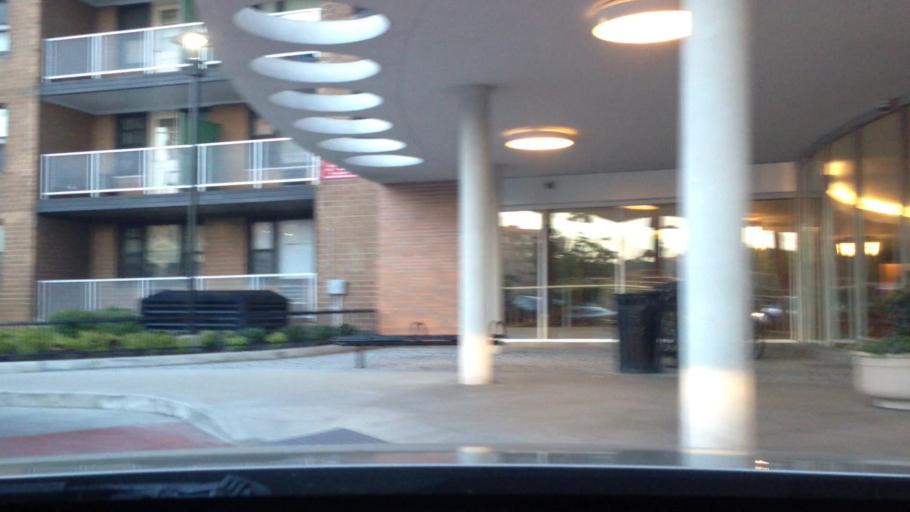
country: US
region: New York
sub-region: Queens County
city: Borough of Queens
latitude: 40.7360
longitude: -73.8605
